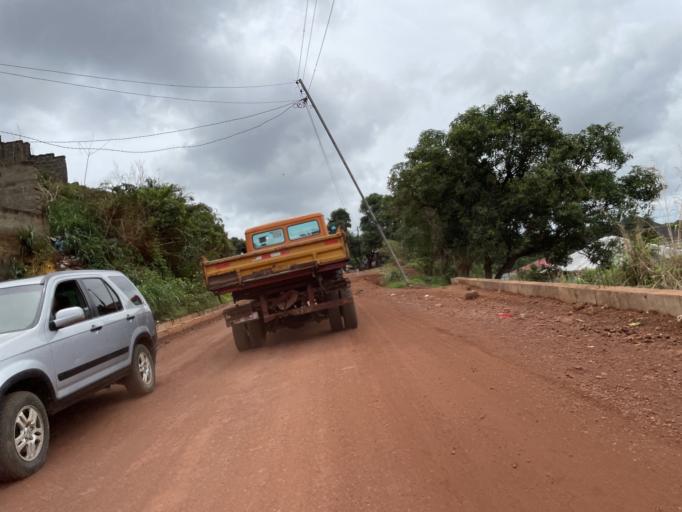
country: SL
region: Western Area
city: Hastings
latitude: 8.3991
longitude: -13.1476
